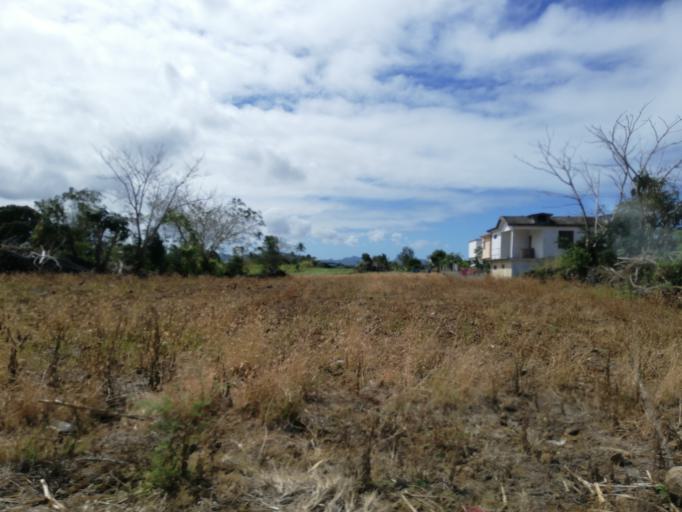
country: MU
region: Grand Port
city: Plaine Magnien
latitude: -20.4573
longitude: 57.6502
